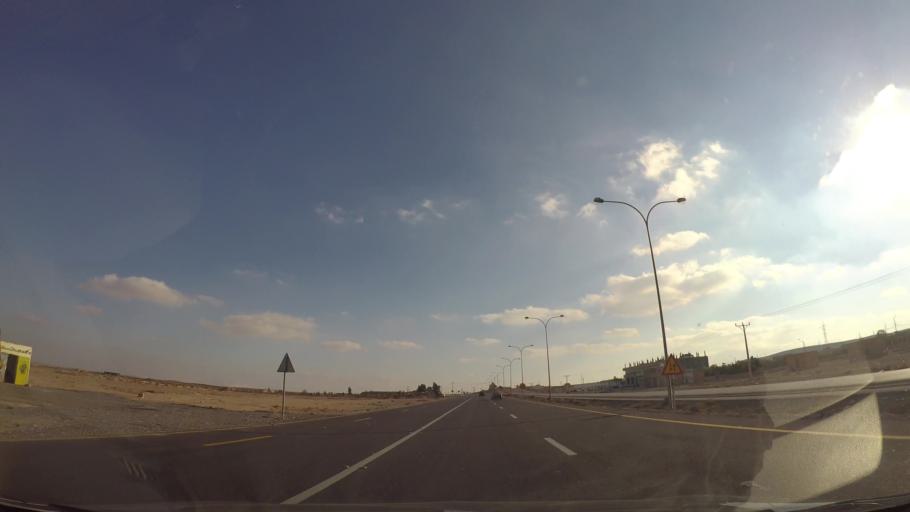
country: JO
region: Karak
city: Karak City
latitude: 31.0897
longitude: 36.0075
